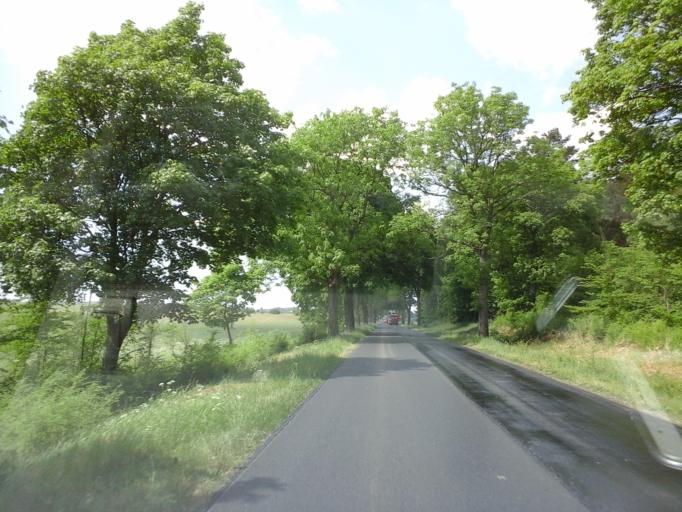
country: PL
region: West Pomeranian Voivodeship
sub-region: Powiat choszczenski
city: Recz
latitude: 53.1897
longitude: 15.6265
